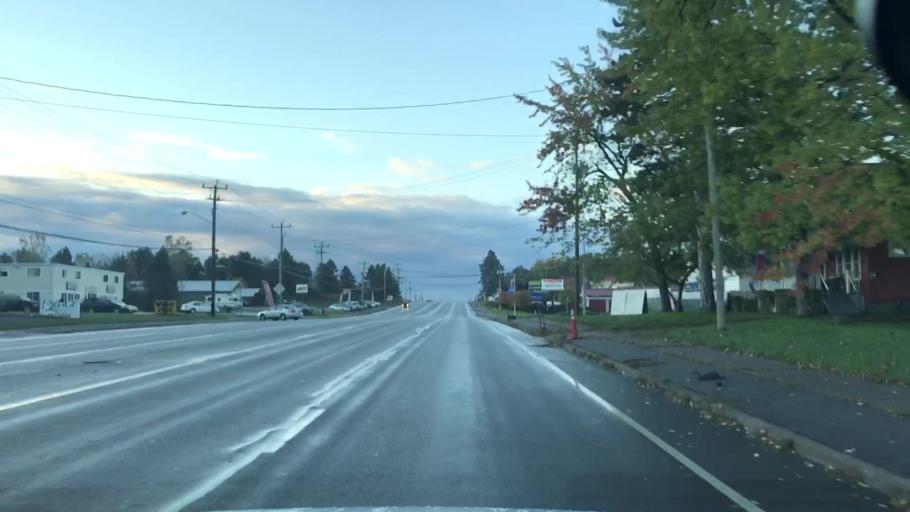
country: US
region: New York
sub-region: Erie County
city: Depew
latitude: 42.8454
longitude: -78.6970
